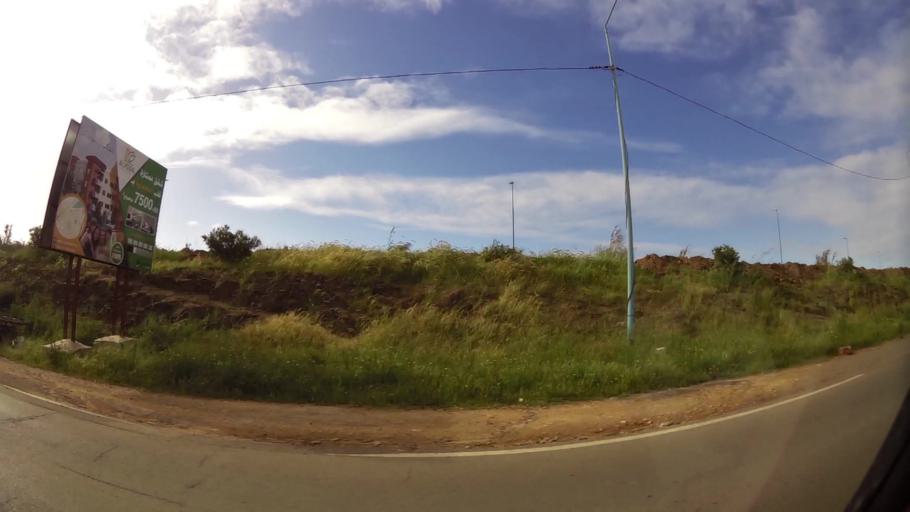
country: MA
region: Grand Casablanca
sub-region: Mohammedia
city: Mohammedia
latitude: 33.7159
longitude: -7.3360
